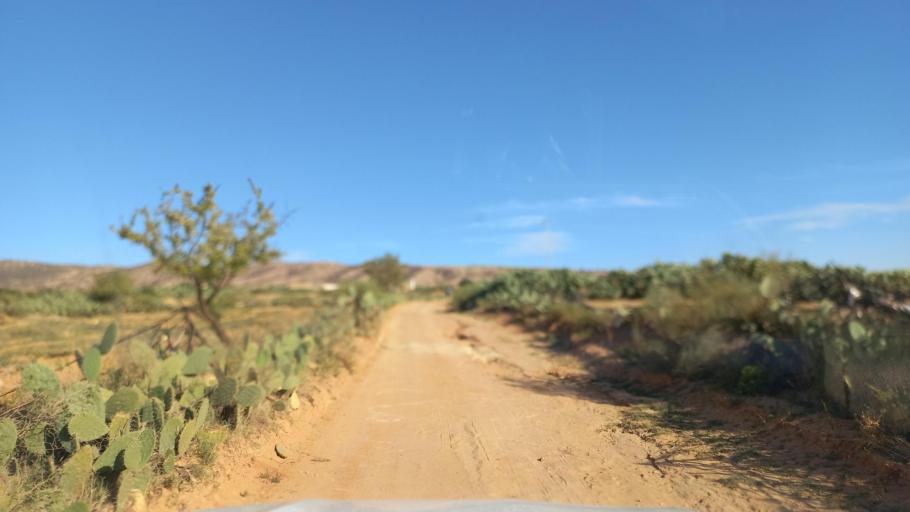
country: TN
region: Al Qasrayn
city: Sbiba
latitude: 35.3297
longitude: 9.1272
